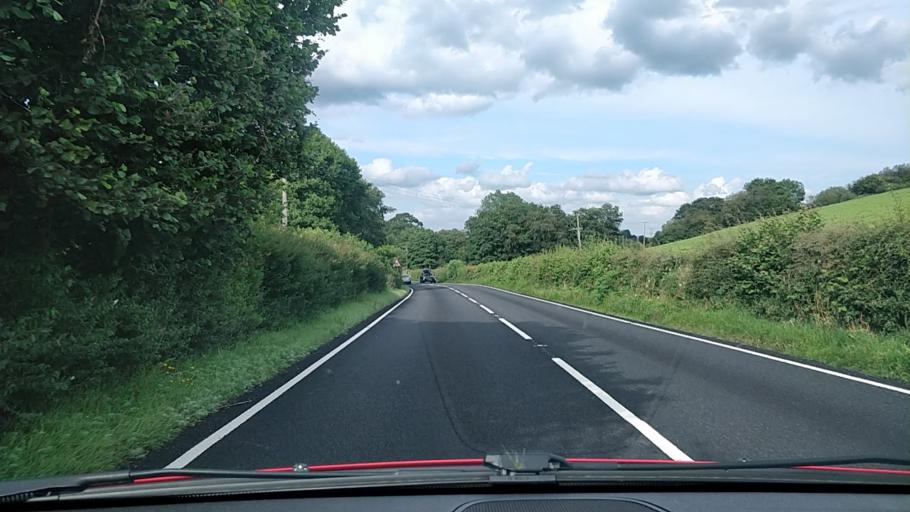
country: GB
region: Wales
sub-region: Denbighshire
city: Llandrillo
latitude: 52.9602
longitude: -3.4796
